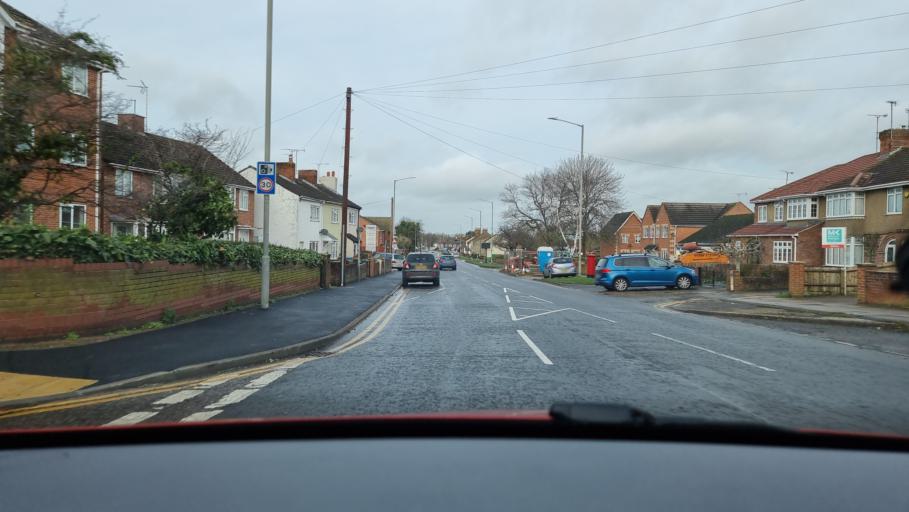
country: GB
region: England
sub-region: Buckinghamshire
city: Aylesbury
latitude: 51.8216
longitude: -0.8150
